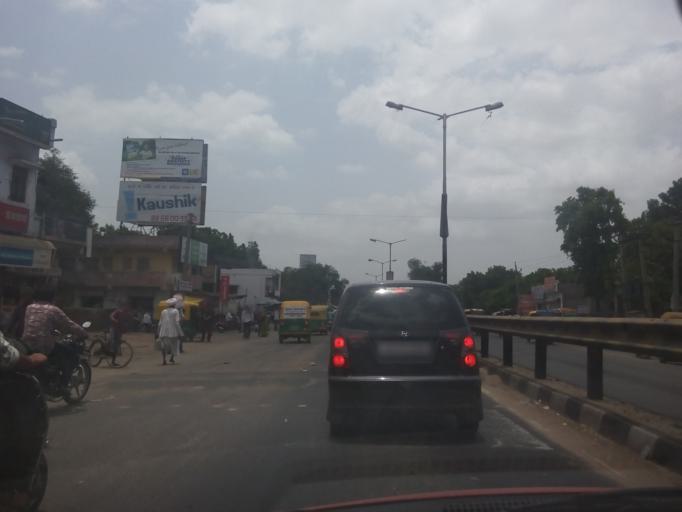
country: IN
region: Gujarat
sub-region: Ahmadabad
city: Sanand
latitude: 22.9913
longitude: 72.3784
